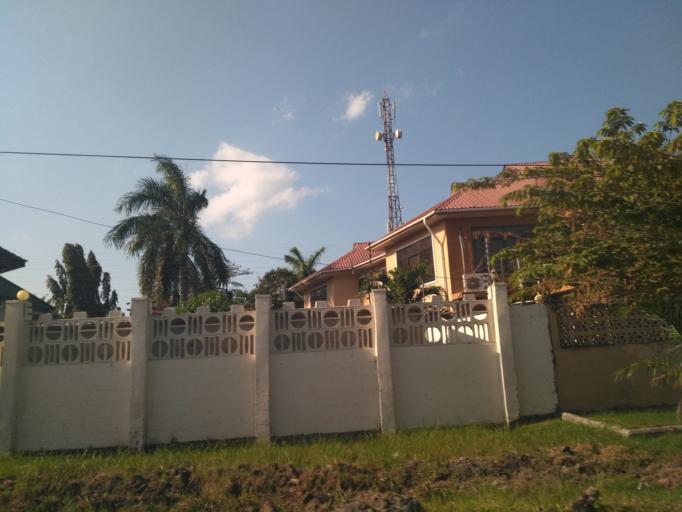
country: TZ
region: Dar es Salaam
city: Magomeni
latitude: -6.7684
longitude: 39.2517
